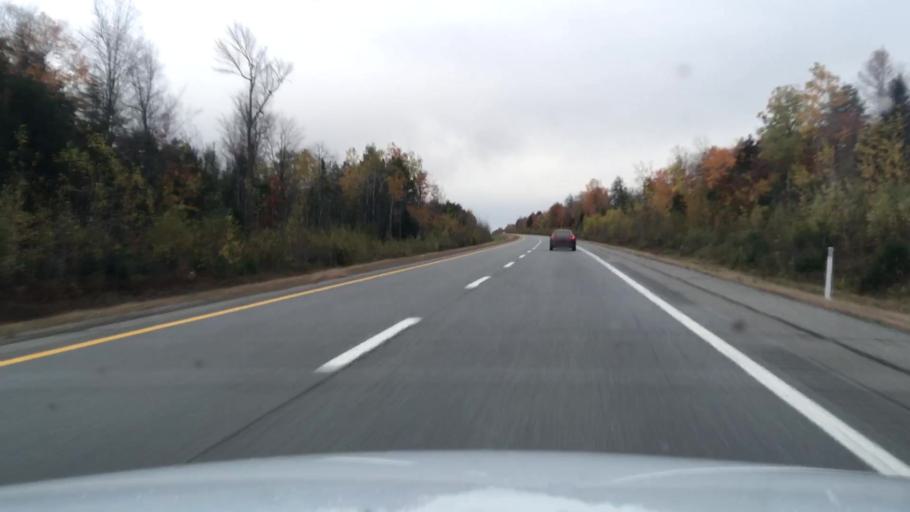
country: US
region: Maine
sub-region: Penobscot County
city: Greenbush
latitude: 45.0980
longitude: -68.6962
